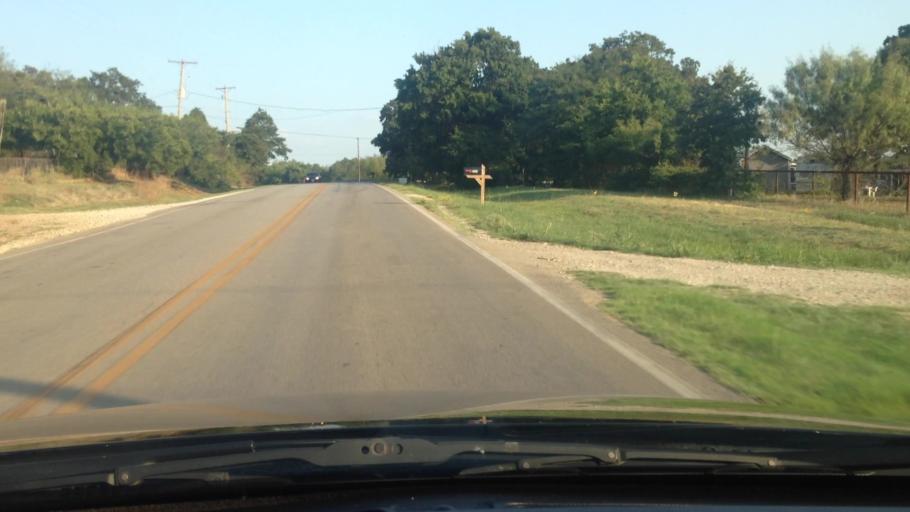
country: US
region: Texas
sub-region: Tarrant County
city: Rendon
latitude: 32.5898
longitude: -97.2508
